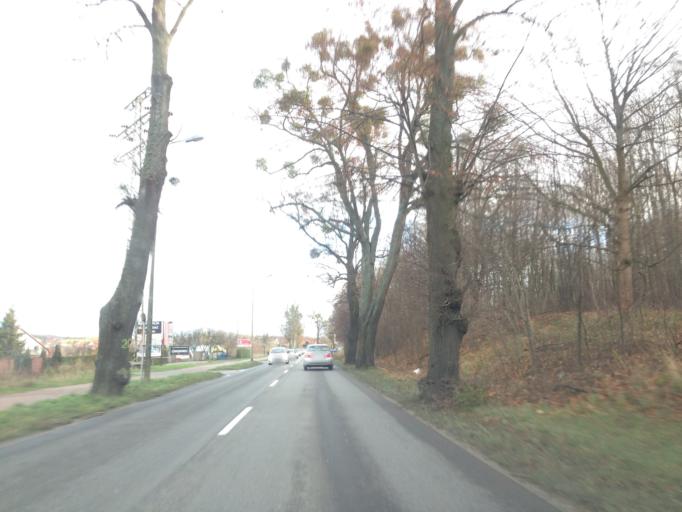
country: PL
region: Pomeranian Voivodeship
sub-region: Powiat gdanski
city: Kolbudy
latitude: 54.2786
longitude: 18.4827
